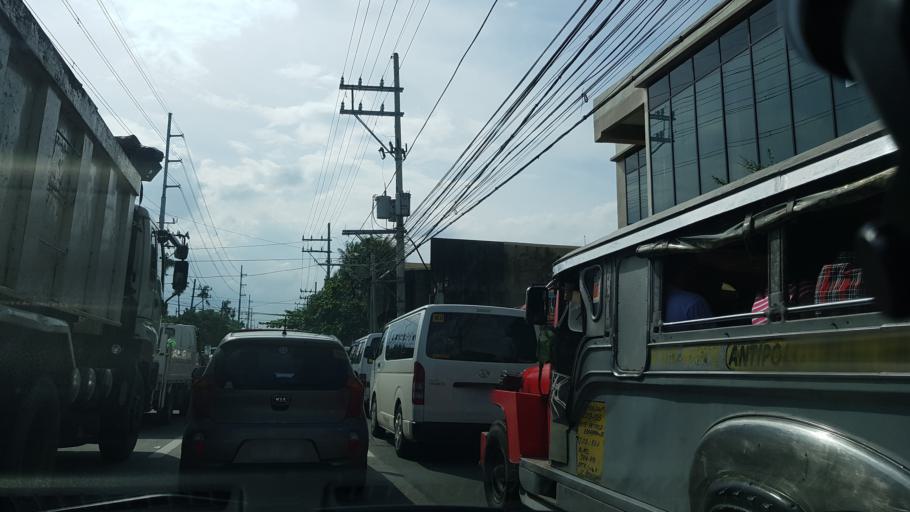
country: PH
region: Calabarzon
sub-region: Province of Rizal
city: Cainta
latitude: 14.5883
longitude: 121.1067
